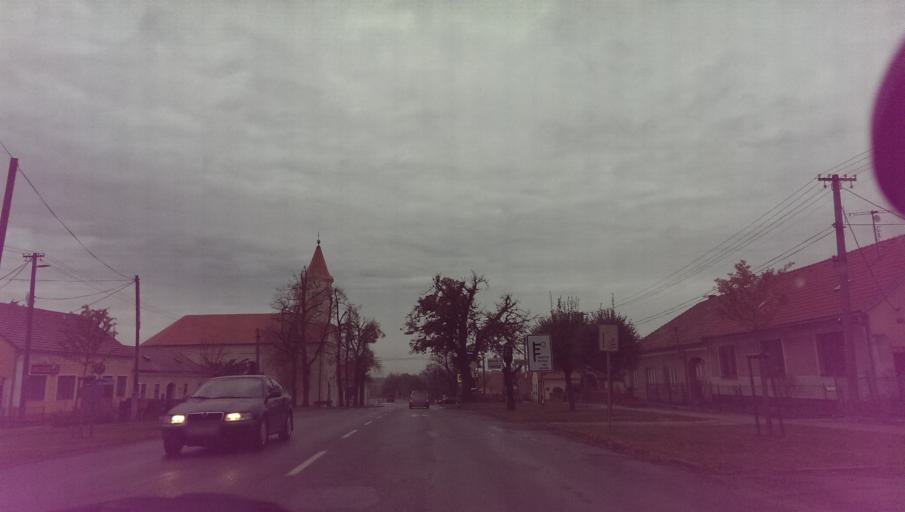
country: AT
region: Lower Austria
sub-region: Politischer Bezirk Hollabrunn
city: Hardegg
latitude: 48.9069
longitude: 15.8700
